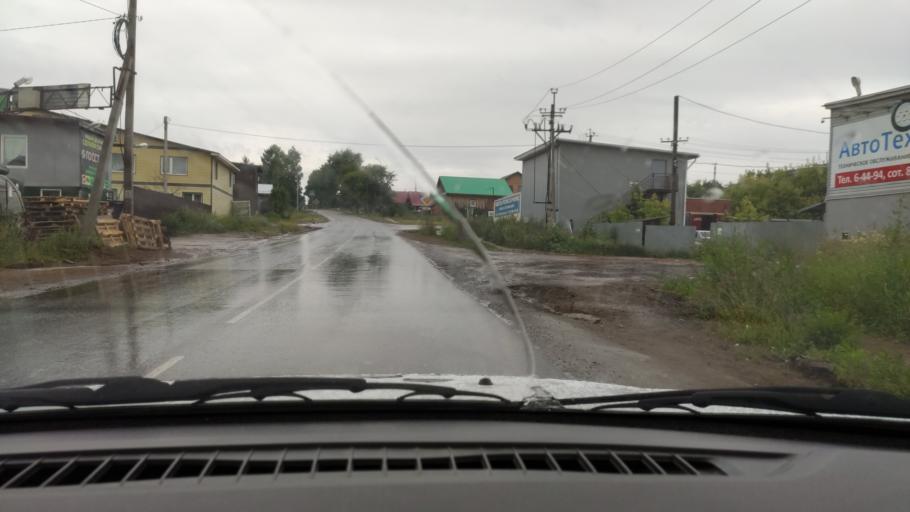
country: RU
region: Udmurtiya
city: Votkinsk
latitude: 57.0669
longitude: 54.0248
